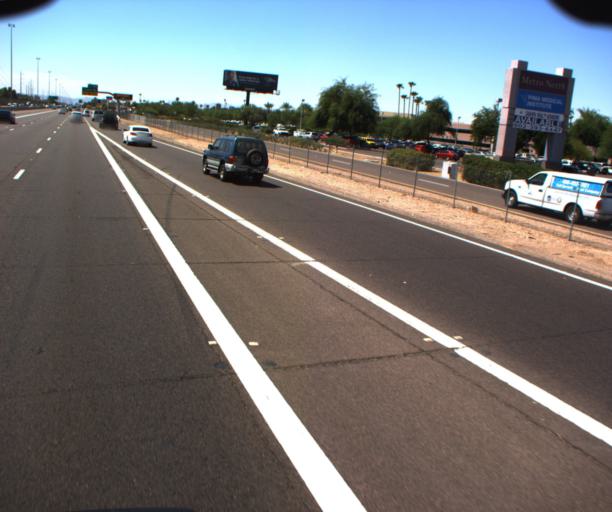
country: US
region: Arizona
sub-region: Maricopa County
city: Glendale
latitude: 33.6078
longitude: -112.1169
